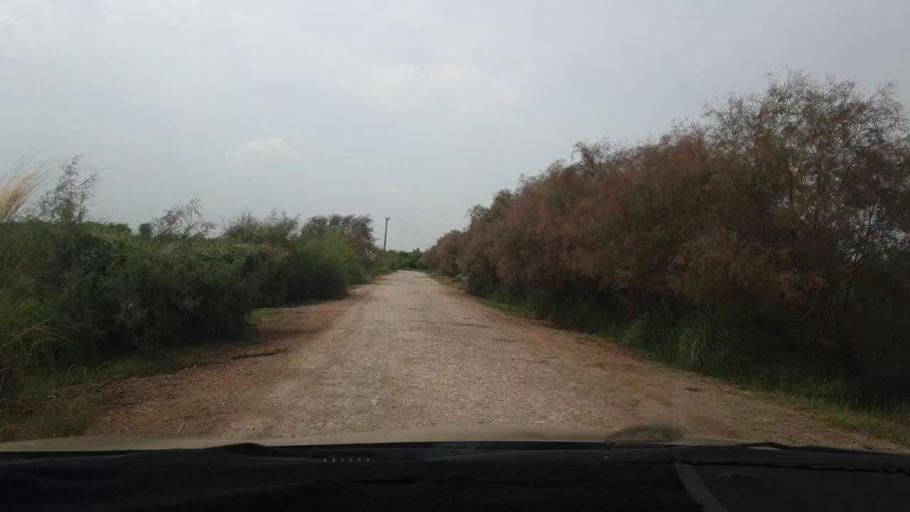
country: PK
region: Sindh
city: Naudero
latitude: 27.6355
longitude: 68.3078
